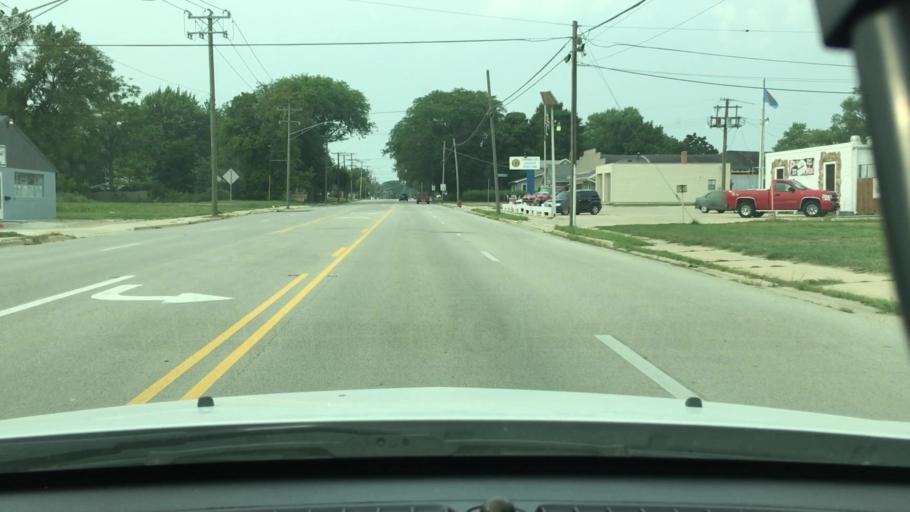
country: US
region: Illinois
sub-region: DeKalb County
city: DeKalb
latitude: 41.9144
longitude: -88.7534
